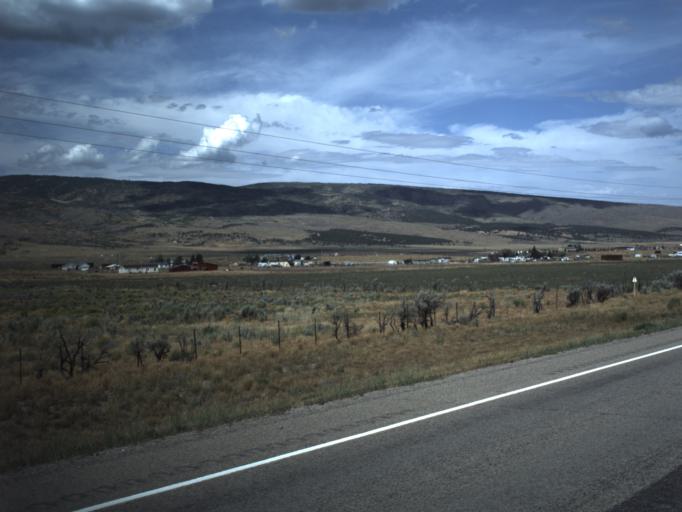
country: US
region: Utah
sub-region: Sanpete County
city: Fairview
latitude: 39.7646
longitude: -111.4845
